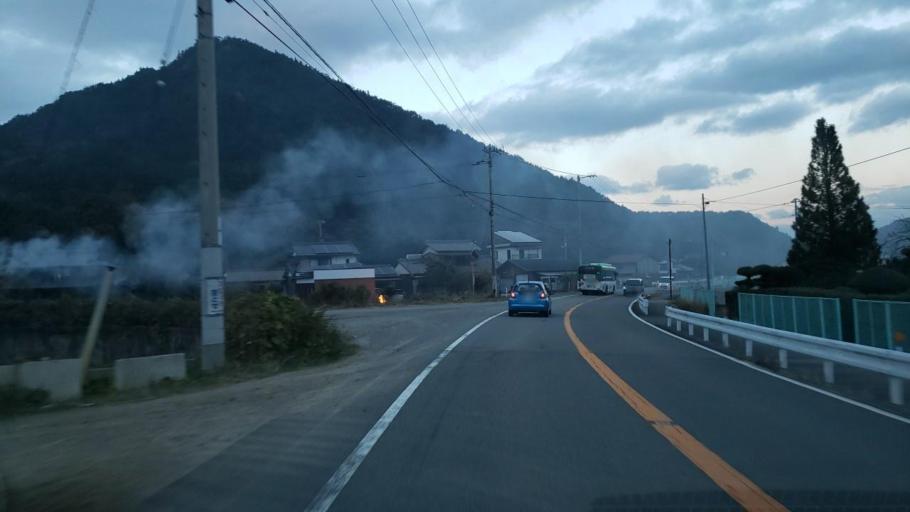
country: JP
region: Tokushima
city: Kamojimacho-jogejima
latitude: 34.2128
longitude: 134.3314
